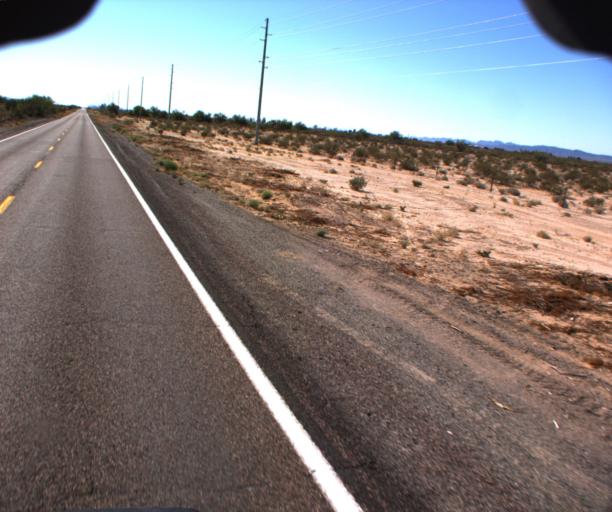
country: US
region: Arizona
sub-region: La Paz County
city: Salome
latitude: 33.8776
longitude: -113.9414
